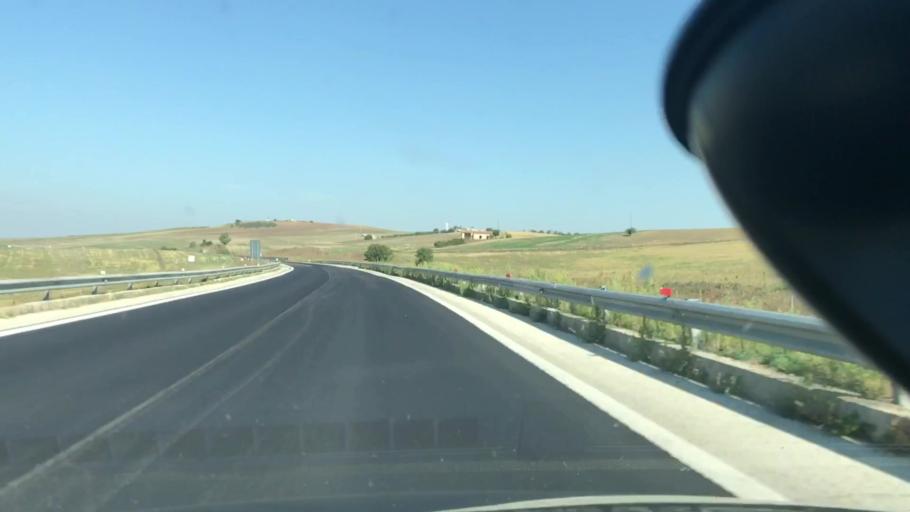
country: IT
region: Apulia
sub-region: Provincia di Barletta - Andria - Trani
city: Spinazzola
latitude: 40.9176
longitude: 16.1011
